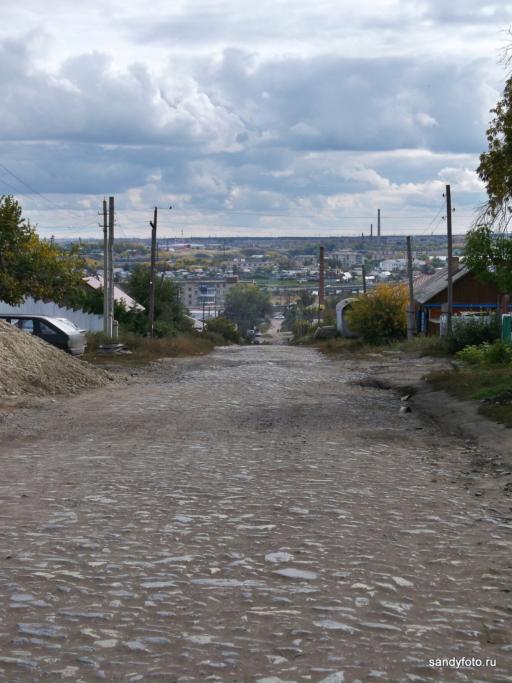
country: RU
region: Chelyabinsk
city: Troitsk
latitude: 54.0997
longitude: 61.5745
